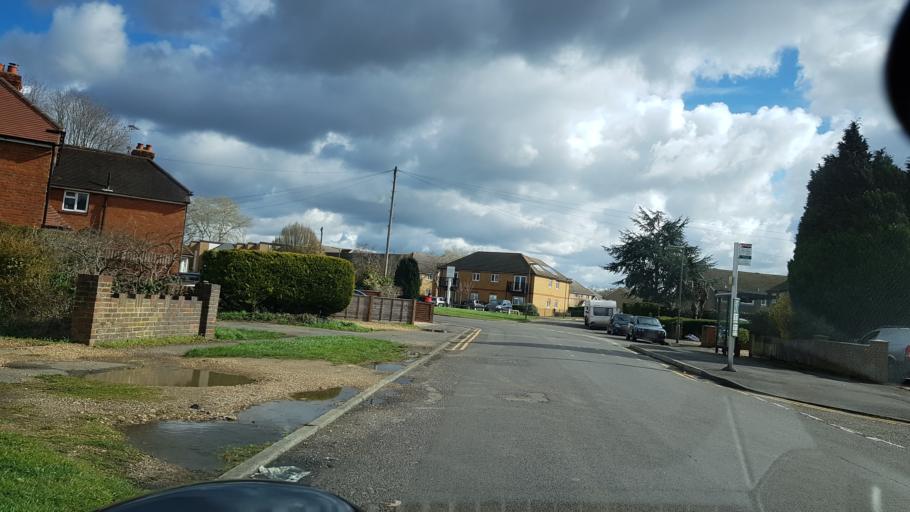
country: GB
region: England
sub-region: Surrey
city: Guildford
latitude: 51.2584
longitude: -0.5691
